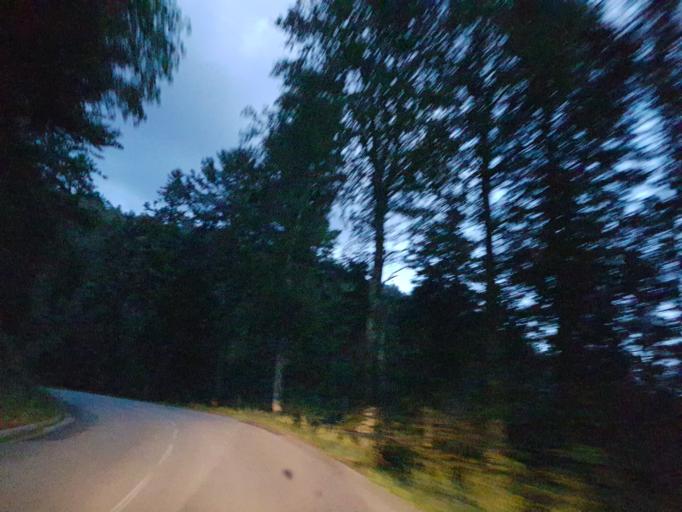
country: FR
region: Lorraine
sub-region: Departement des Vosges
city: Xonrupt-Longemer
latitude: 48.0629
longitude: 6.9954
